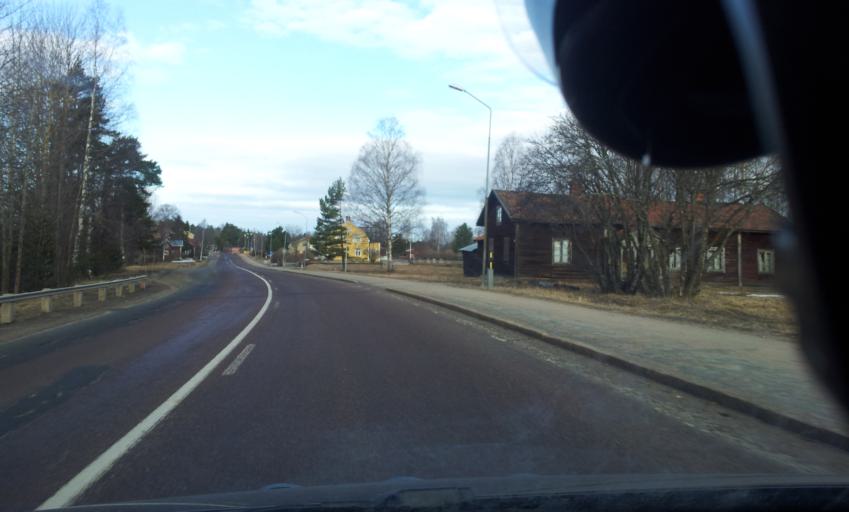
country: SE
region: Gaevleborg
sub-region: Ljusdals Kommun
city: Ljusdal
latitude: 61.8371
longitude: 16.0615
